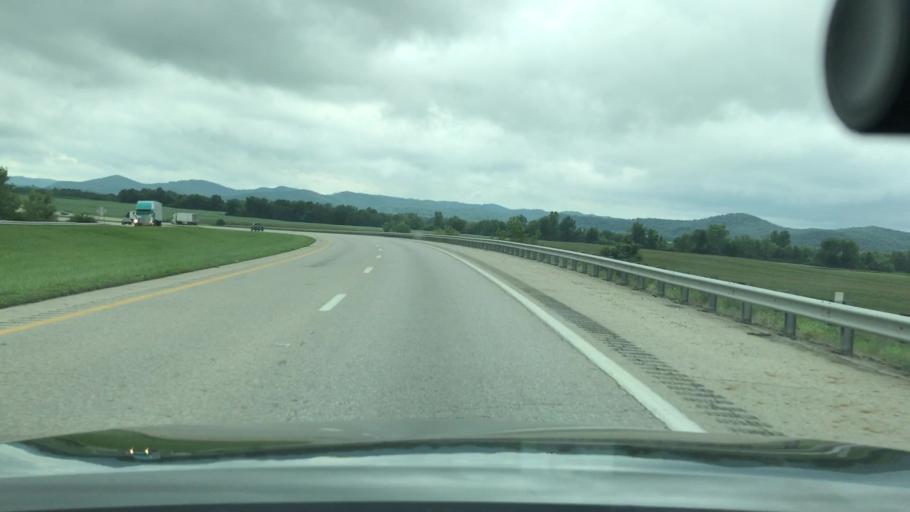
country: US
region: Ohio
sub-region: Ross County
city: Chillicothe
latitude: 39.2751
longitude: -82.8844
